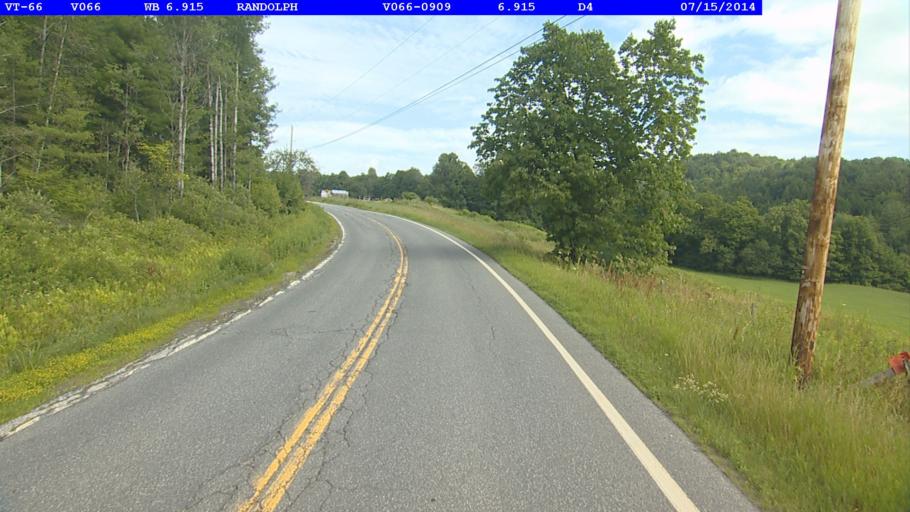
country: US
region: Vermont
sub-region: Orange County
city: Randolph
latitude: 43.9476
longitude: -72.5614
